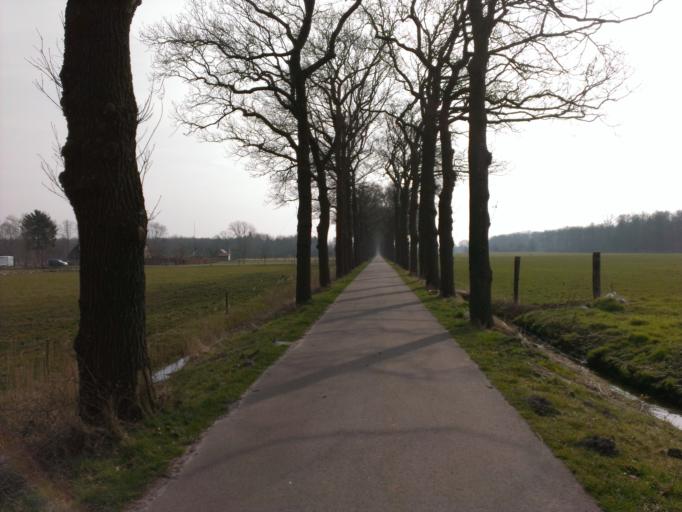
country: NL
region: Drenthe
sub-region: Gemeente Hoogeveen
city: Hoogeveen
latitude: 52.7460
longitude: 6.5044
